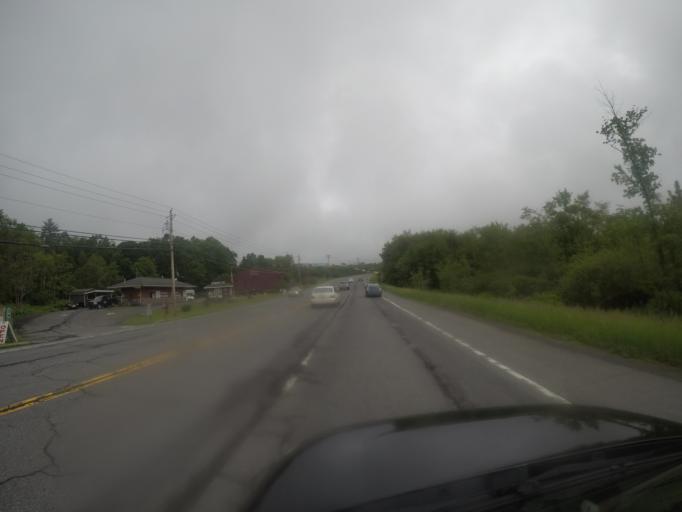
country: US
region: New York
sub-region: Ulster County
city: West Hurley
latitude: 41.9781
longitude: -74.0848
